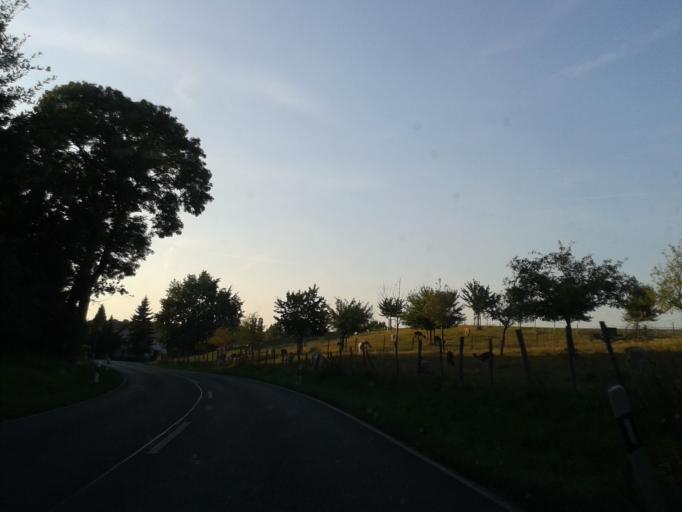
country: DE
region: Saxony
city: Klipphausen
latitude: 51.1009
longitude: 13.4909
